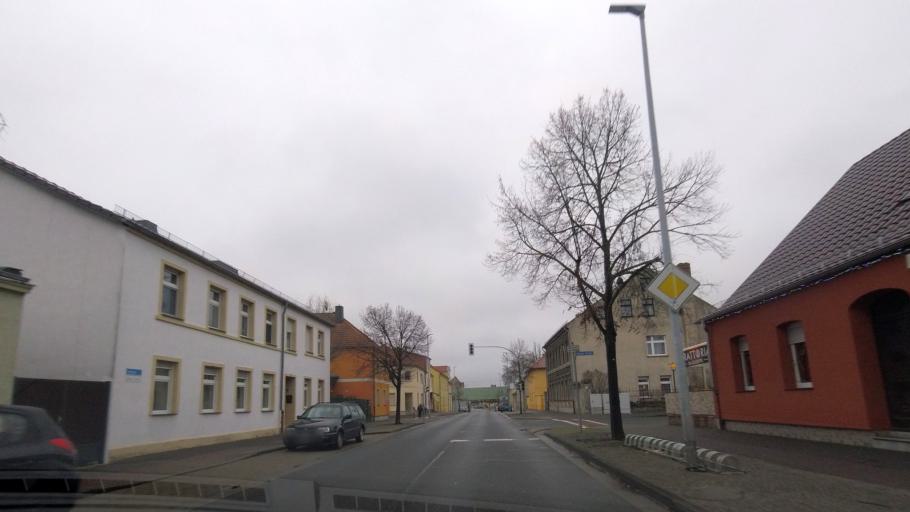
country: DE
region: Brandenburg
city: Luckenwalde
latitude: 52.0910
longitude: 13.1574
